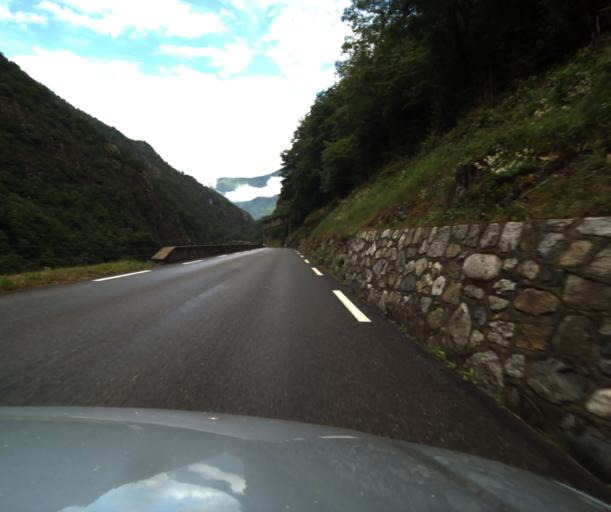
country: FR
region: Midi-Pyrenees
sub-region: Departement des Hautes-Pyrenees
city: Luz-Saint-Sauveur
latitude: 42.8445
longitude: -0.0072
